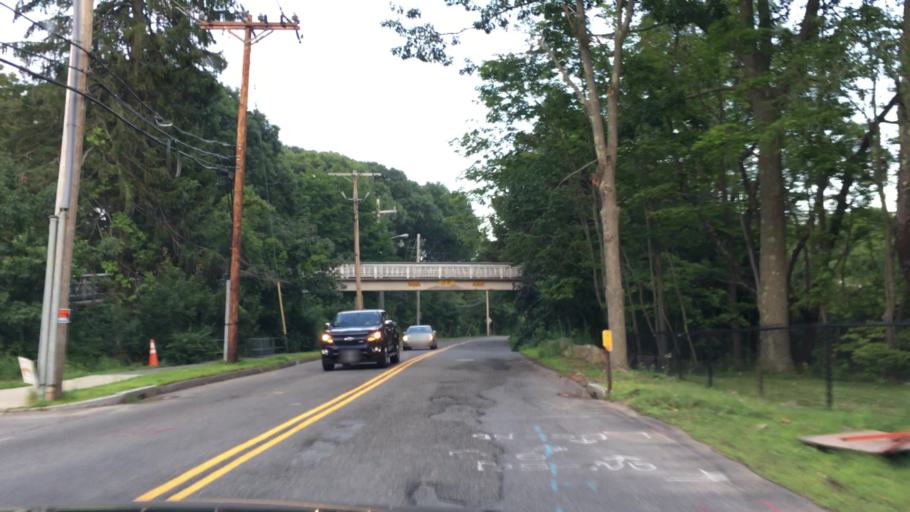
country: US
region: Massachusetts
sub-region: Essex County
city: Essex
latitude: 42.5805
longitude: -70.7653
